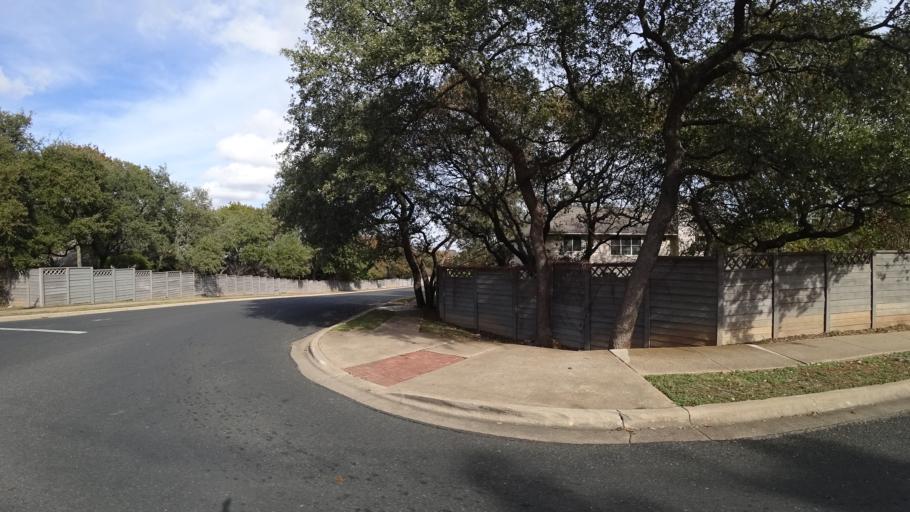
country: US
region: Texas
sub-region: Williamson County
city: Brushy Creek
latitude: 30.5127
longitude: -97.7435
